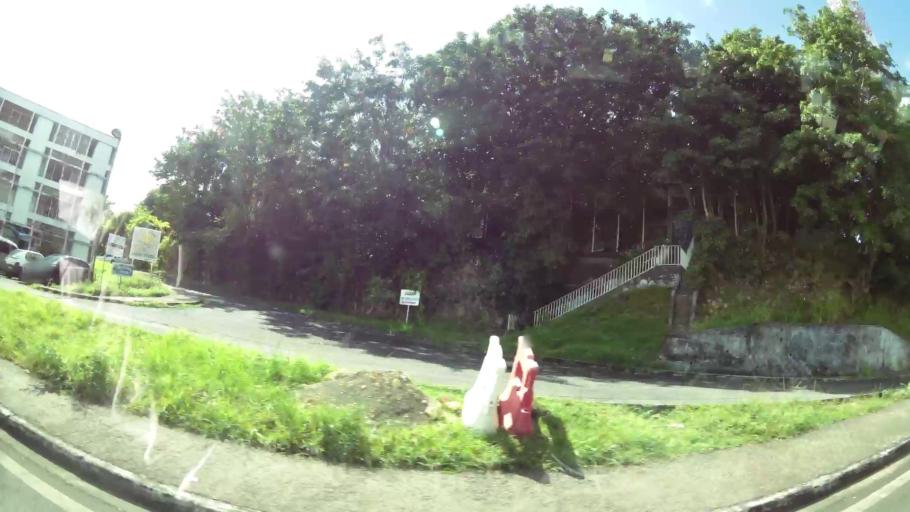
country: GP
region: Guadeloupe
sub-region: Guadeloupe
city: Pointe-a-Pitre
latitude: 16.2495
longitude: -61.5365
